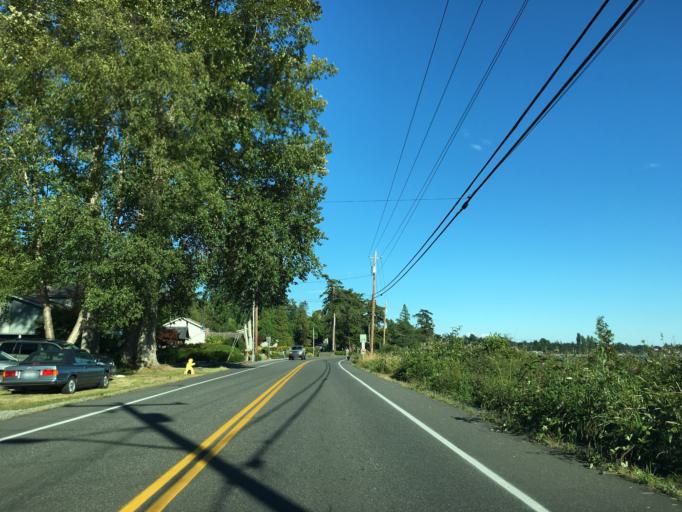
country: US
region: Washington
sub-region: Whatcom County
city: Birch Bay
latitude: 48.9392
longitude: -122.7564
